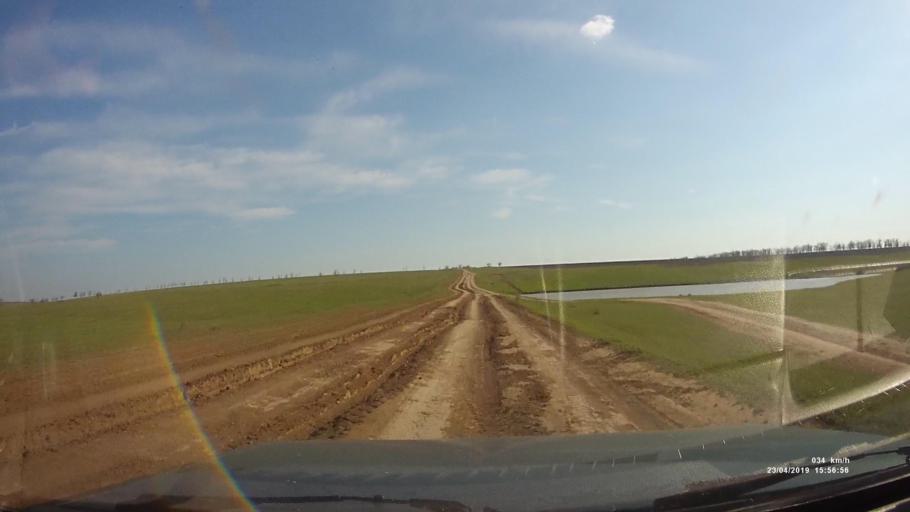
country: RU
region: Rostov
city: Remontnoye
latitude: 46.5346
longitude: 43.1106
